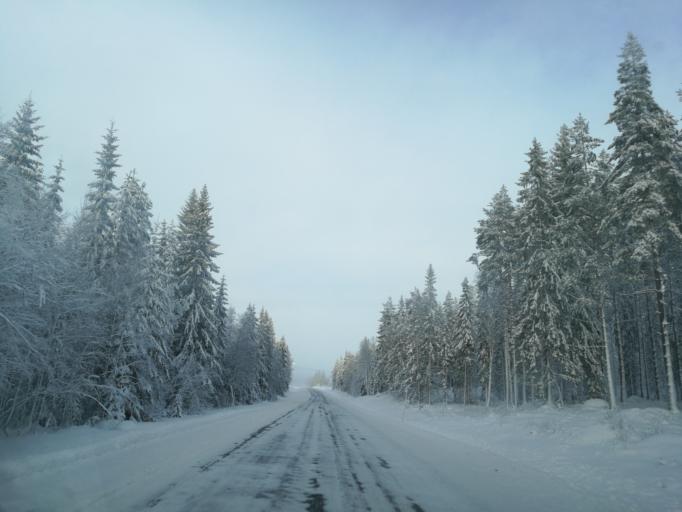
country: SE
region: Vaermland
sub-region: Torsby Kommun
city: Torsby
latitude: 60.6181
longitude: 12.7150
